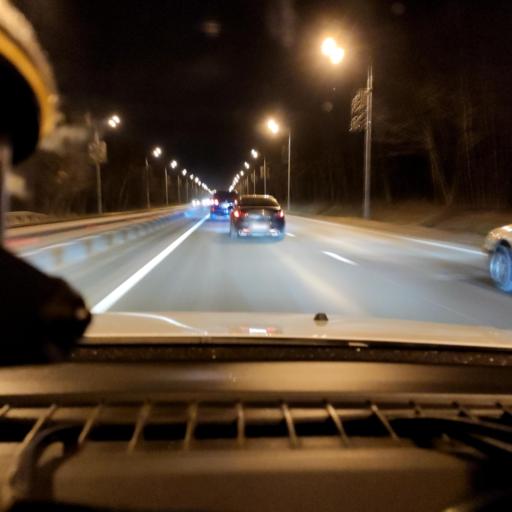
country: RU
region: Samara
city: Novosemeykino
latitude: 53.3303
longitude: 50.2314
